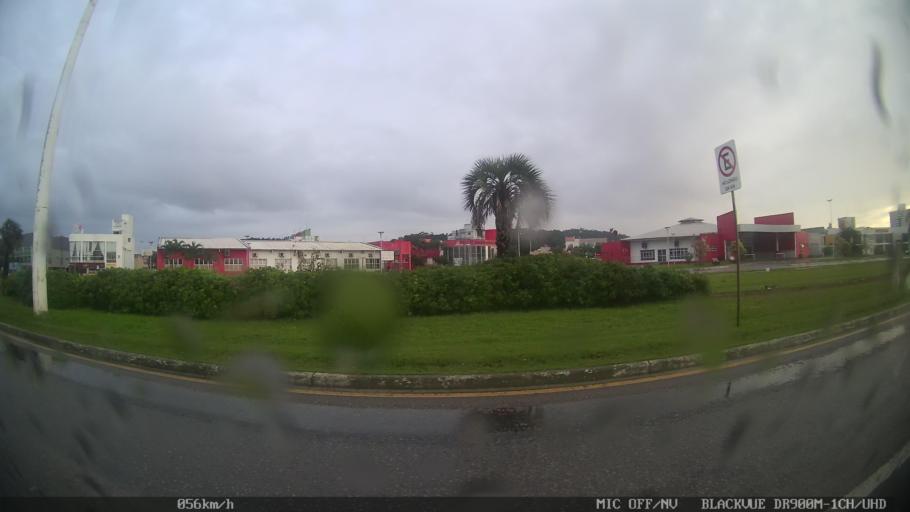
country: BR
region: Santa Catarina
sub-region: Sao Jose
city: Campinas
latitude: -27.6057
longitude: -48.6221
